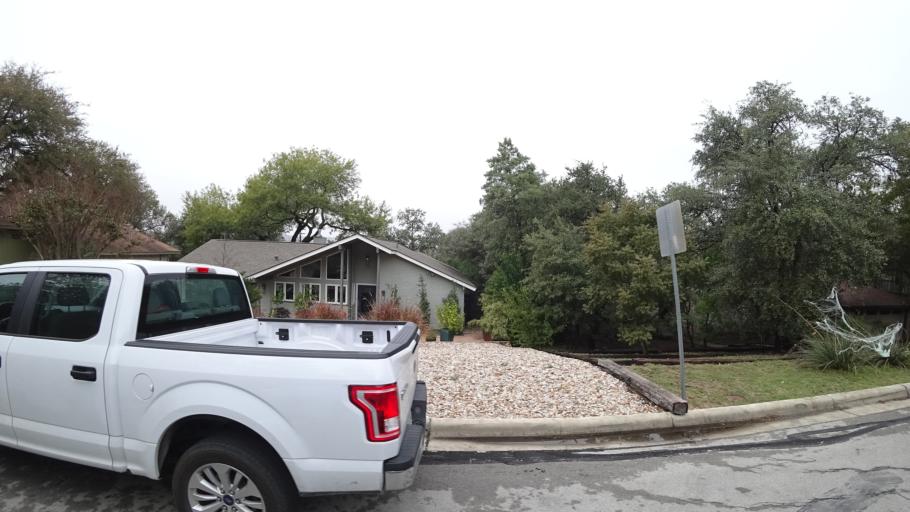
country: US
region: Texas
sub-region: Travis County
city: Rollingwood
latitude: 30.2569
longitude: -97.7791
